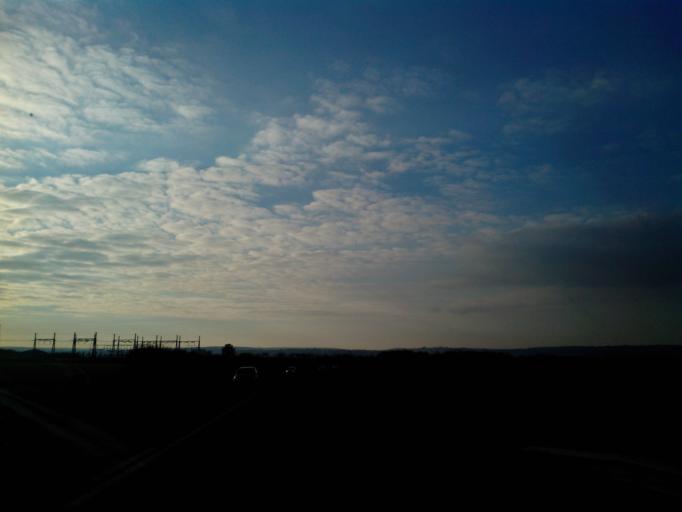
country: FR
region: Picardie
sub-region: Departement de la Somme
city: Salouel
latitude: 49.8595
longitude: 2.2580
